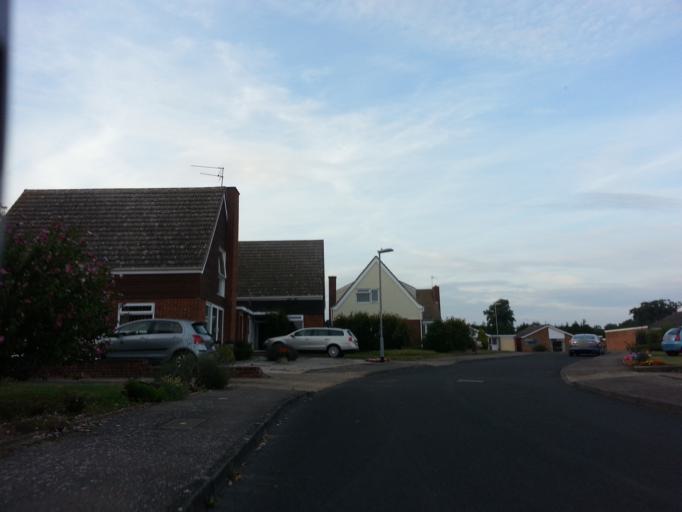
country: GB
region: England
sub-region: Suffolk
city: Ipswich
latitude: 52.0410
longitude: 1.1324
